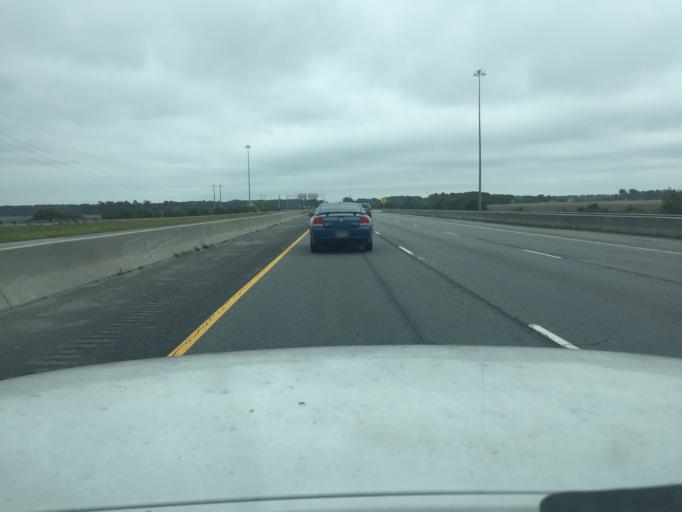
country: US
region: Georgia
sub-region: Chatham County
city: Georgetown
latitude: 31.9844
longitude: -81.1990
